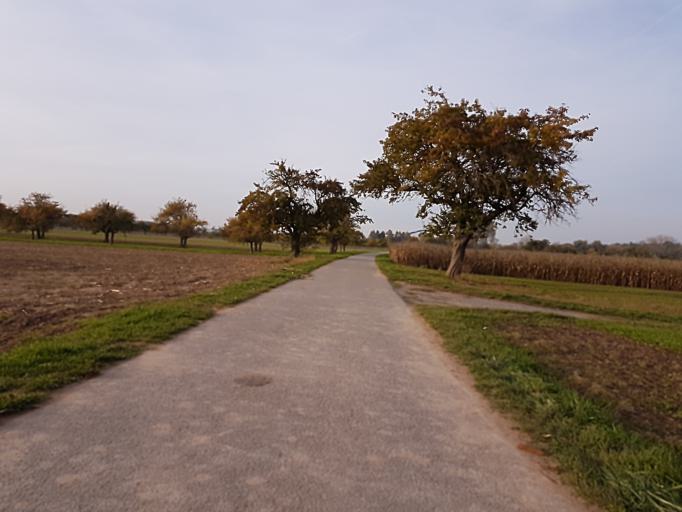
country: DE
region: Bavaria
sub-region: Regierungsbezirk Unterfranken
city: Grosswallstadt
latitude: 49.8892
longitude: 9.1549
